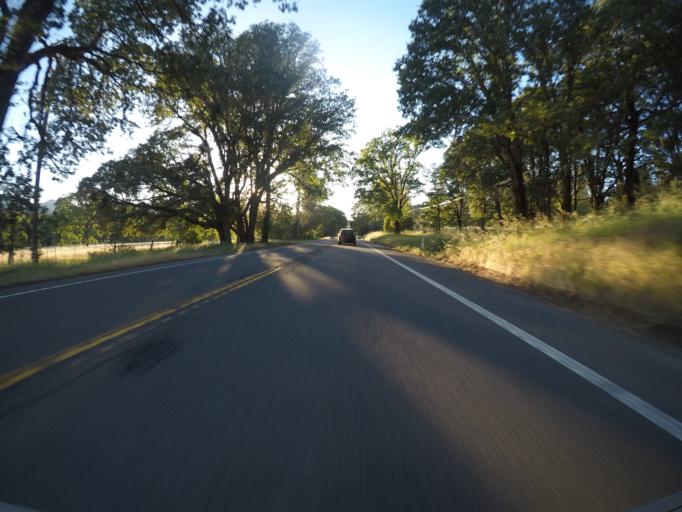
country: US
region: California
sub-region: Mendocino County
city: Laytonville
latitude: 39.7422
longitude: -123.5181
